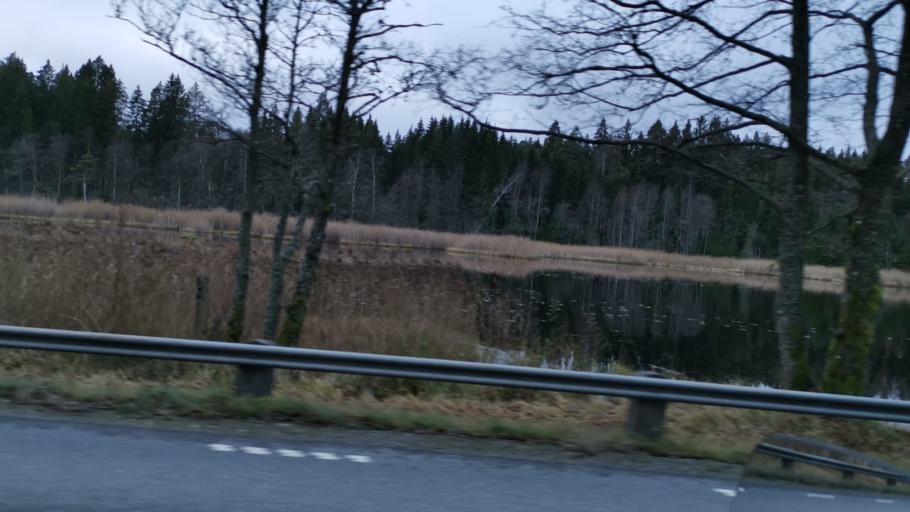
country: SE
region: Vaestra Goetaland
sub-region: Orust
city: Henan
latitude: 58.2317
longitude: 11.6927
